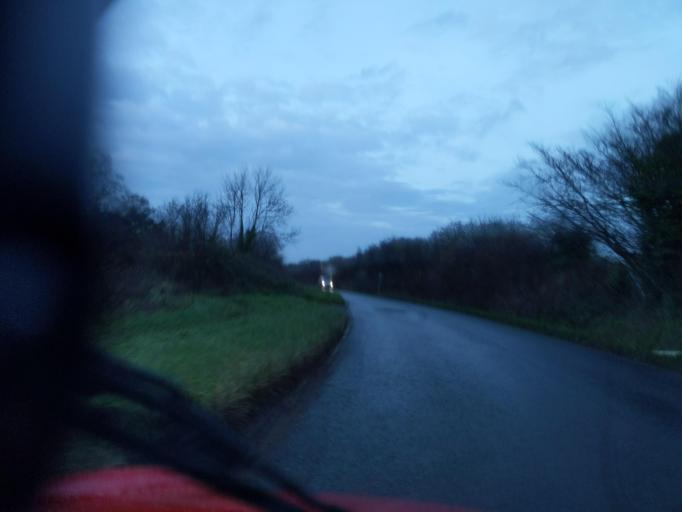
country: GB
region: England
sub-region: Plymouth
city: Plymstock
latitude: 50.3445
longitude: -4.0760
